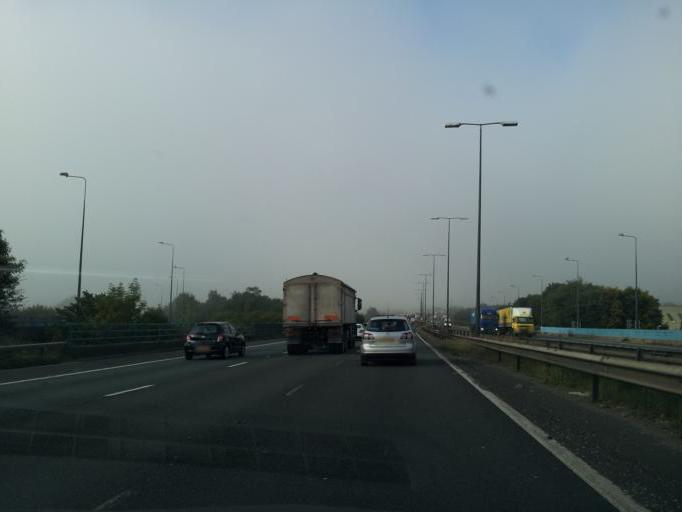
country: GB
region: England
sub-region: Borough of Rochdale
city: Milnrow
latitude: 53.6038
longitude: -2.1055
